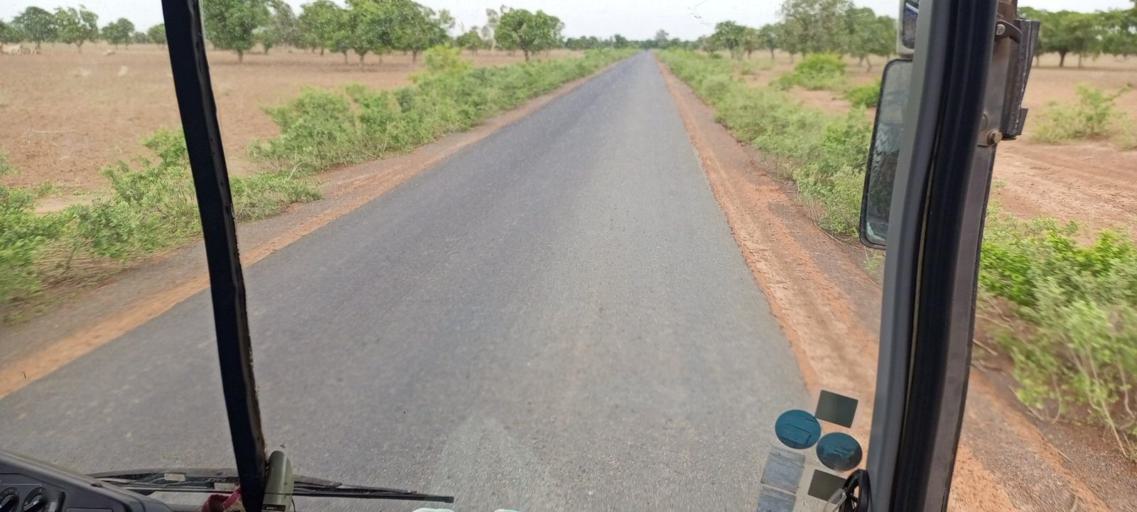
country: ML
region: Segou
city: Bla
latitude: 12.7459
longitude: -5.7310
